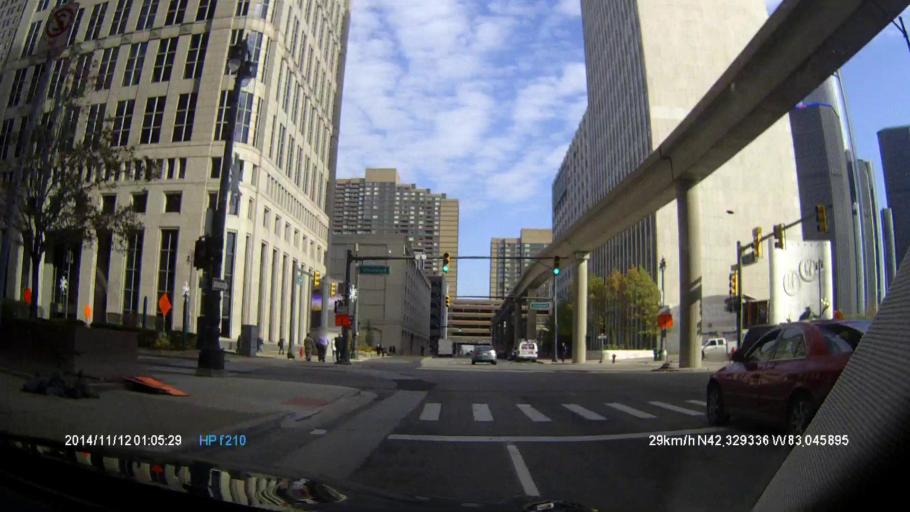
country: US
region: Michigan
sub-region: Wayne County
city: Detroit
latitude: 42.3293
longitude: -83.0454
